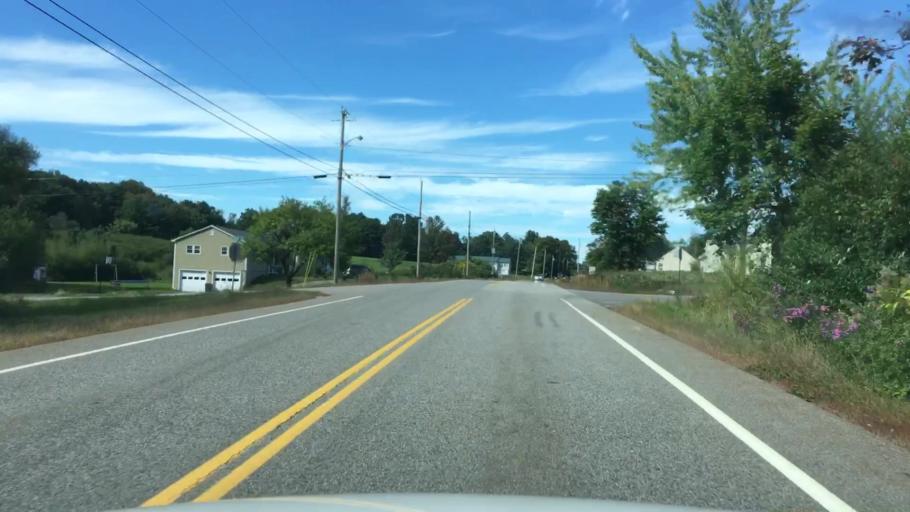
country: US
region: Maine
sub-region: Cumberland County
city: Westbrook
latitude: 43.6670
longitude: -70.4071
